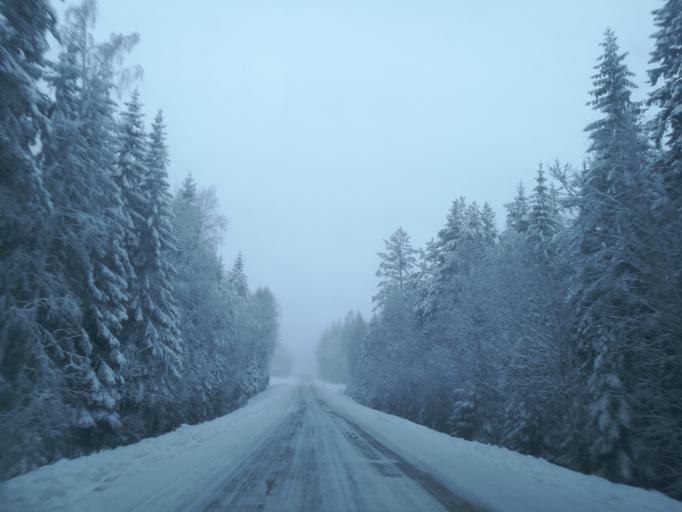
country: NO
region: Hedmark
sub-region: Grue
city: Kirkenaer
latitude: 60.5434
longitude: 12.5484
